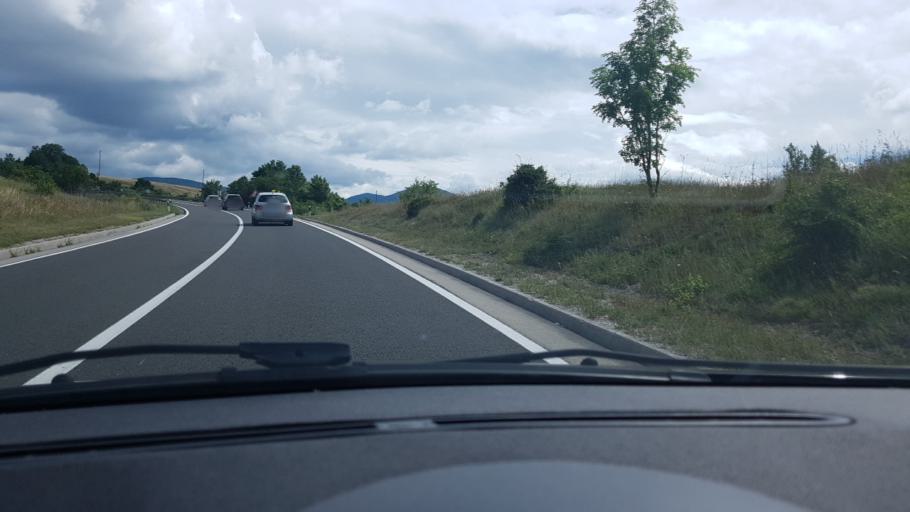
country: HR
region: Zadarska
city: Gracac
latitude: 44.4914
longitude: 15.7622
